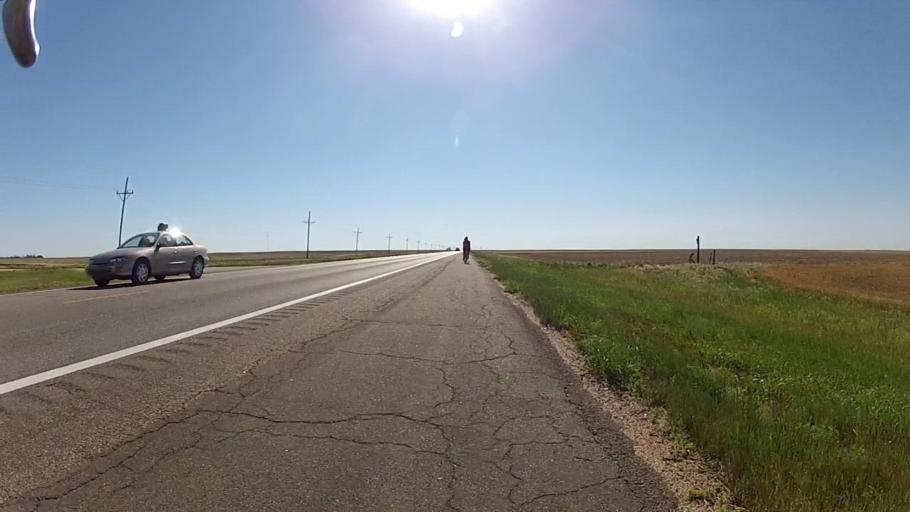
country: US
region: Kansas
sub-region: Kiowa County
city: Greensburg
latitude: 37.5862
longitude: -99.6311
